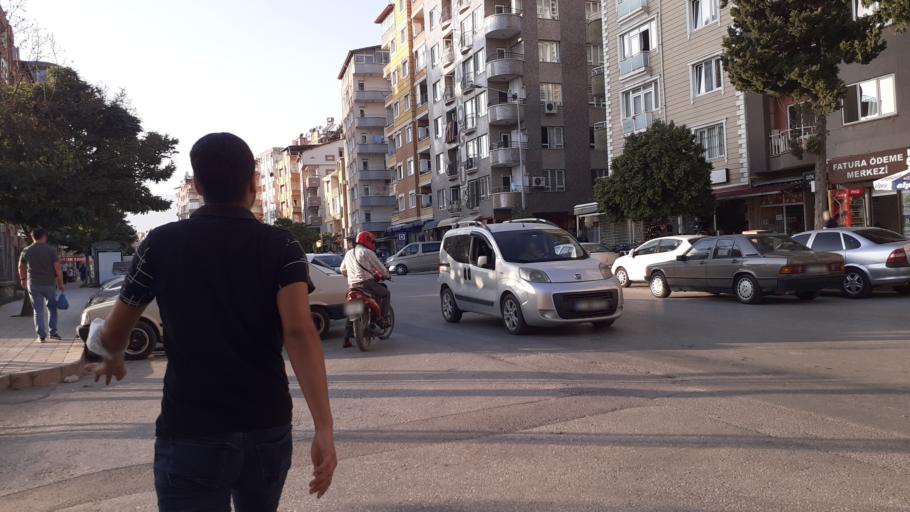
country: TR
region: Hatay
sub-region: Antakya Ilcesi
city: Antakya
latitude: 36.2072
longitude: 36.1515
